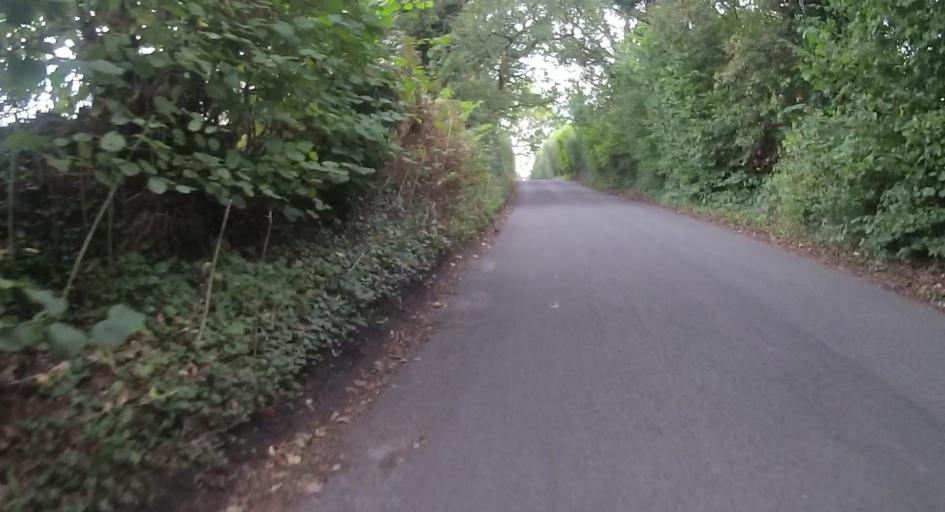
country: GB
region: England
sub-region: Hampshire
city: Odiham
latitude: 51.2942
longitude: -0.9014
